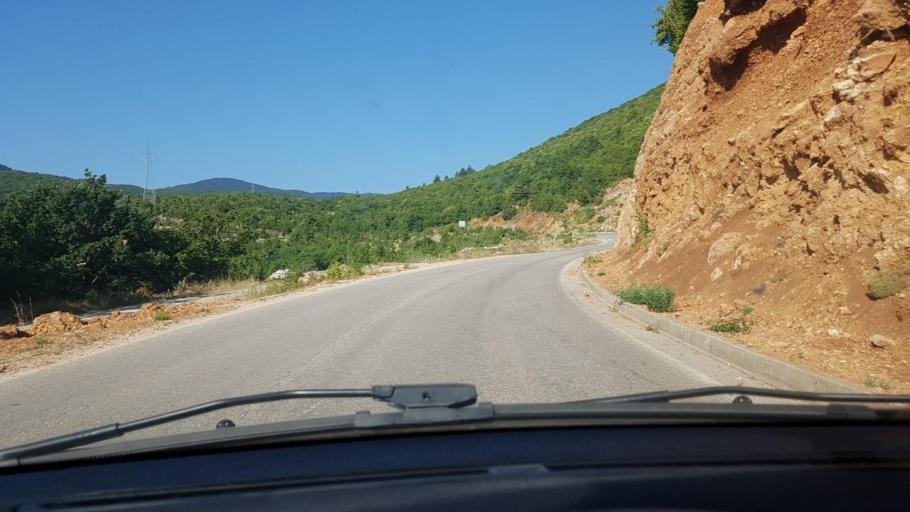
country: BA
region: Federation of Bosnia and Herzegovina
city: Rumboci
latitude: 43.8235
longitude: 17.4778
